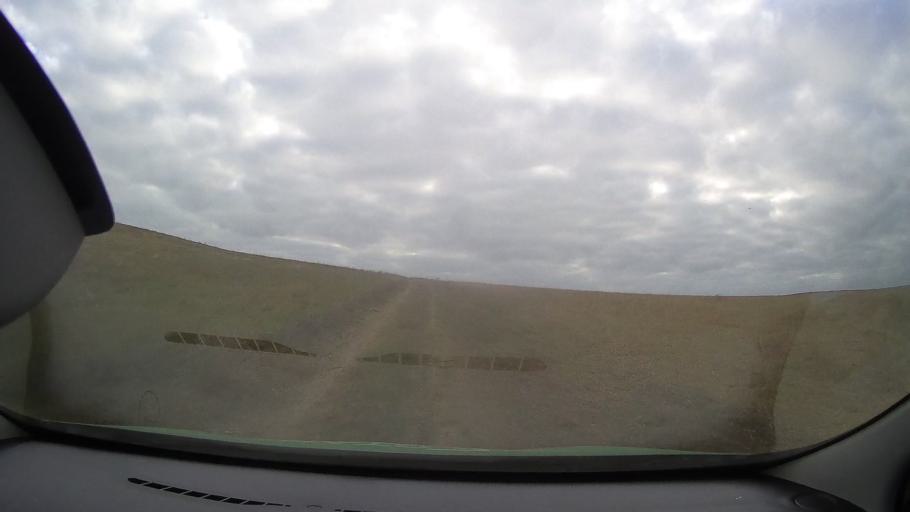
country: RO
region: Tulcea
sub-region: Comuna Jurilovca
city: Jurilovca
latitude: 44.7659
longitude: 28.9226
